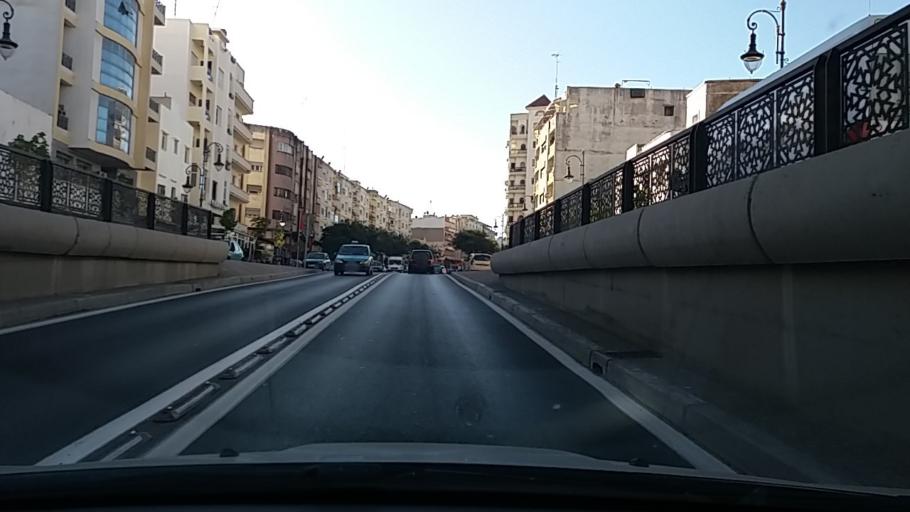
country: MA
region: Tanger-Tetouan
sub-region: Tanger-Assilah
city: Tangier
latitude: 35.7727
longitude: -5.8155
